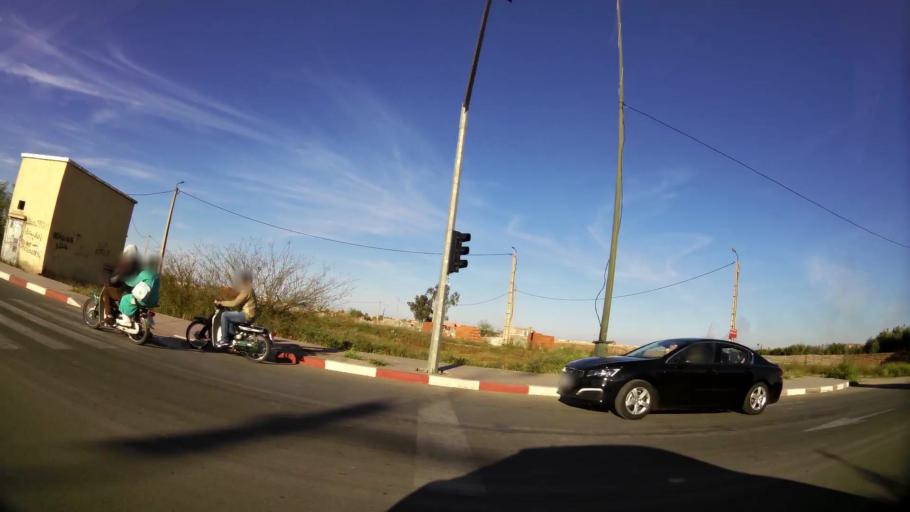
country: MA
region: Marrakech-Tensift-Al Haouz
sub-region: Marrakech
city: Marrakesh
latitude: 31.6666
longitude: -8.0570
